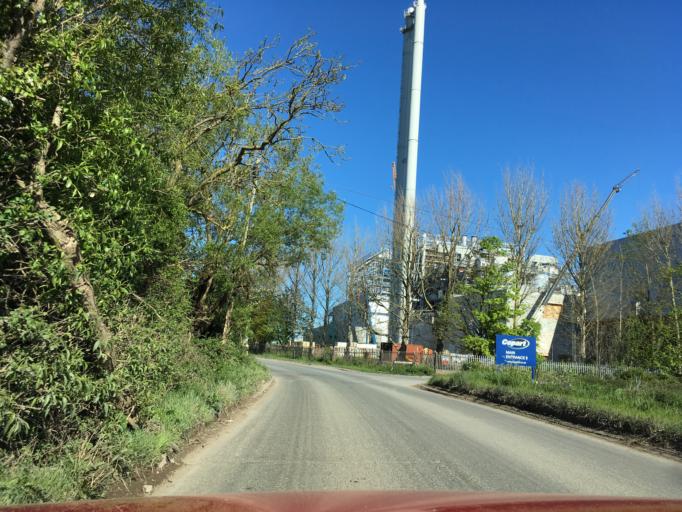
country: GB
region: England
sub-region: South Gloucestershire
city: Severn Beach
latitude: 51.5307
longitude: -2.6653
